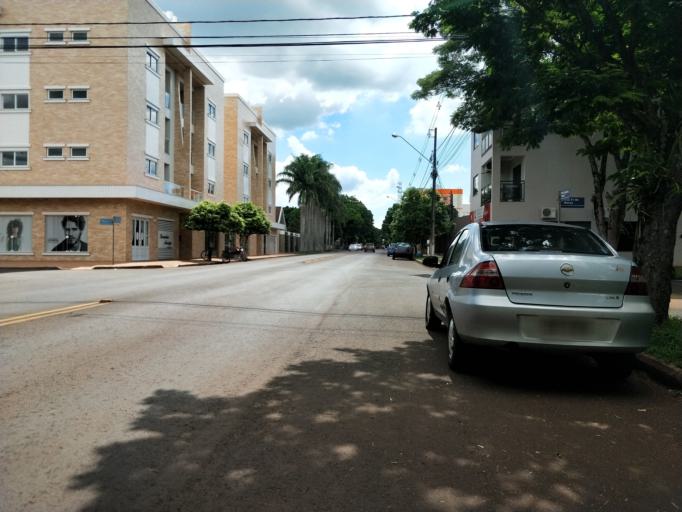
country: BR
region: Parana
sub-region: Marechal Candido Rondon
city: Marechal Candido Rondon
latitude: -24.5605
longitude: -54.0513
